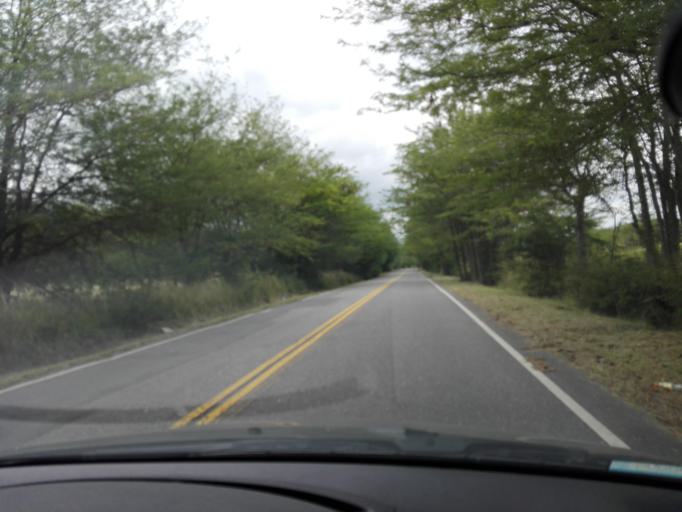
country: AR
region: Cordoba
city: Cuesta Blanca
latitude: -31.5972
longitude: -64.5647
